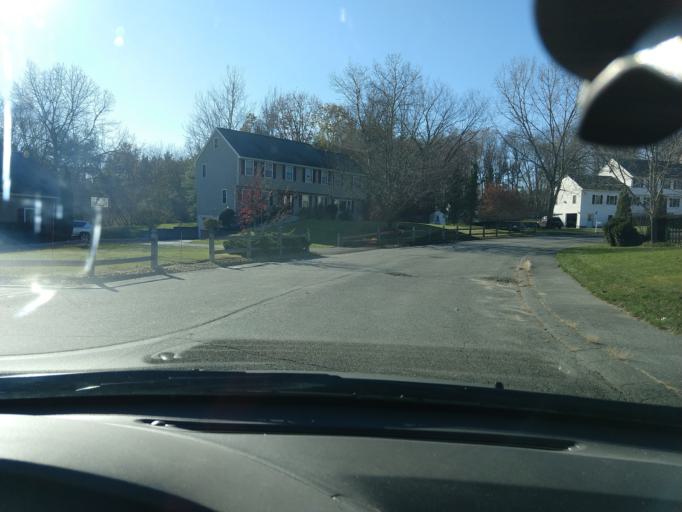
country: US
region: Massachusetts
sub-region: Middlesex County
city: East Pepperell
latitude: 42.6828
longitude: -71.5593
